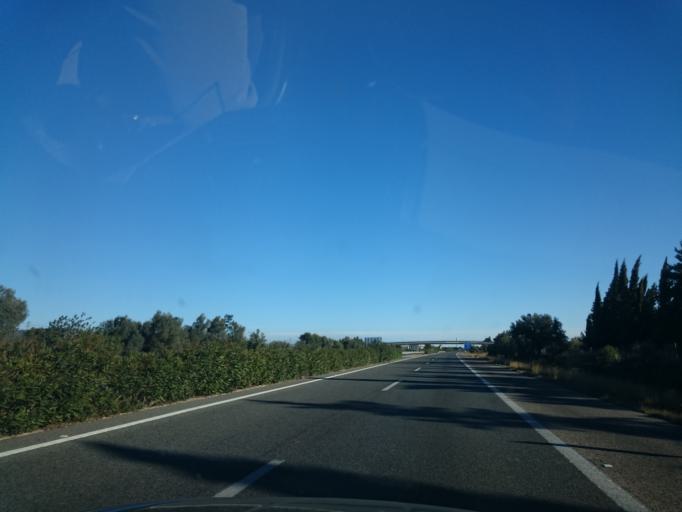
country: ES
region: Catalonia
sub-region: Provincia de Tarragona
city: Camarles
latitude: 40.7791
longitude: 0.6447
